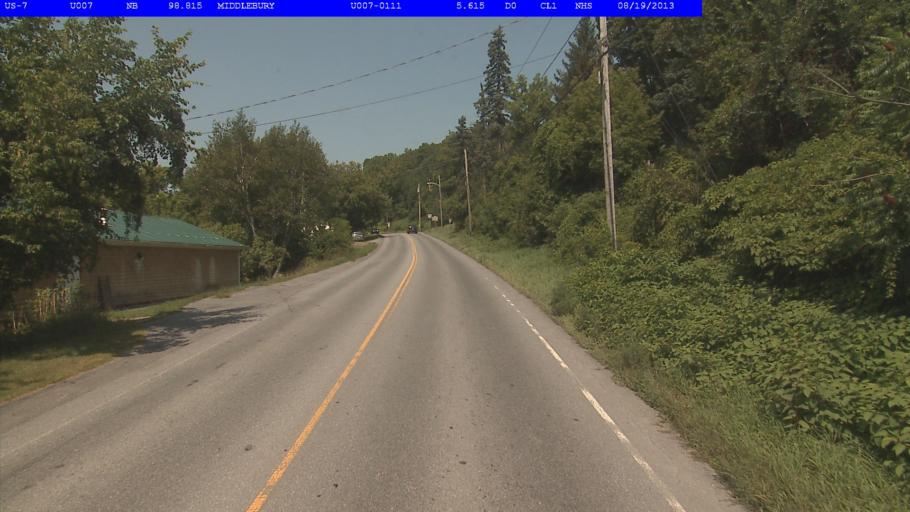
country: US
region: Vermont
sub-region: Addison County
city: Middlebury (village)
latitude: 44.0217
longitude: -73.1653
